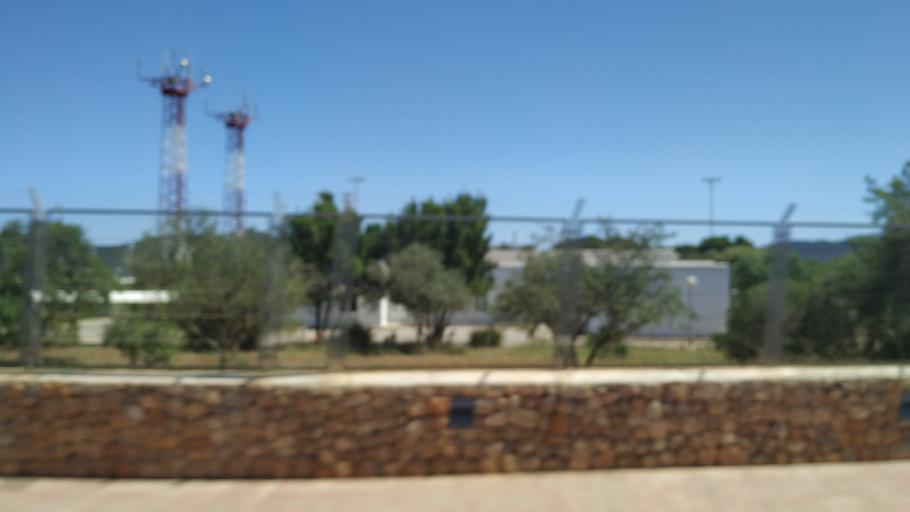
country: ES
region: Balearic Islands
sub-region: Illes Balears
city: Ibiza
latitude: 38.8800
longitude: 1.3719
